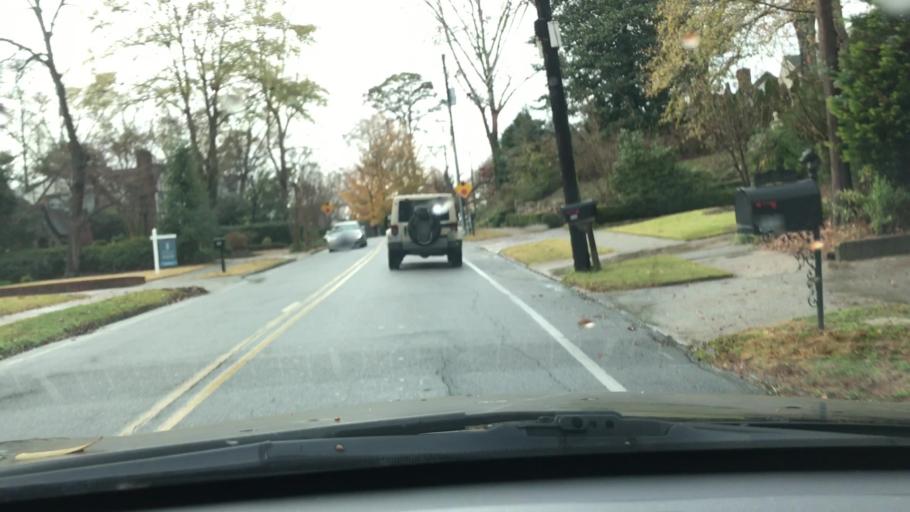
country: US
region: Georgia
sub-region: DeKalb County
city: Druid Hills
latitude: 33.7974
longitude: -84.3563
